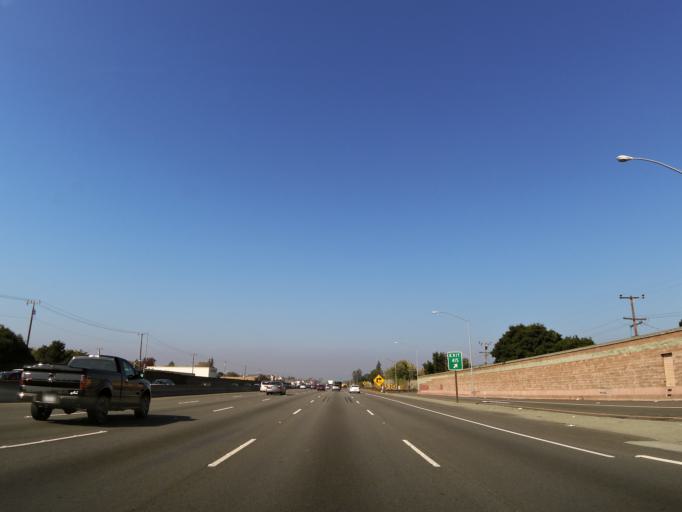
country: US
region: California
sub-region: San Mateo County
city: San Mateo
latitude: 37.5616
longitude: -122.3037
